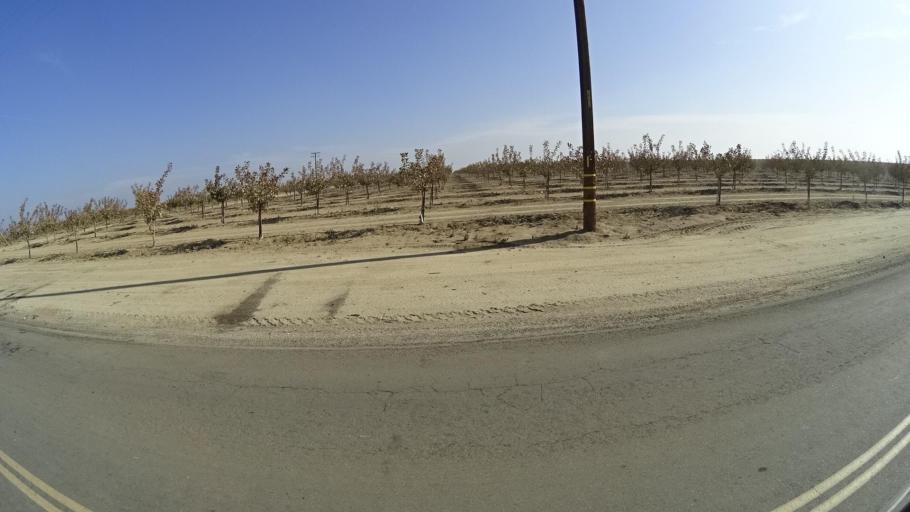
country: US
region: California
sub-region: Kern County
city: McFarland
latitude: 35.6163
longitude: -119.1688
